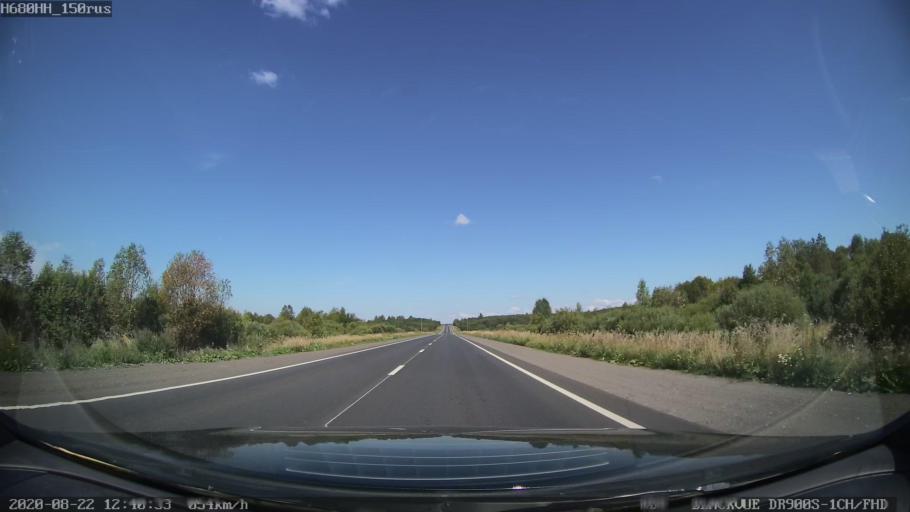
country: RU
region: Tverskaya
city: Rameshki
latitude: 57.3359
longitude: 36.0949
